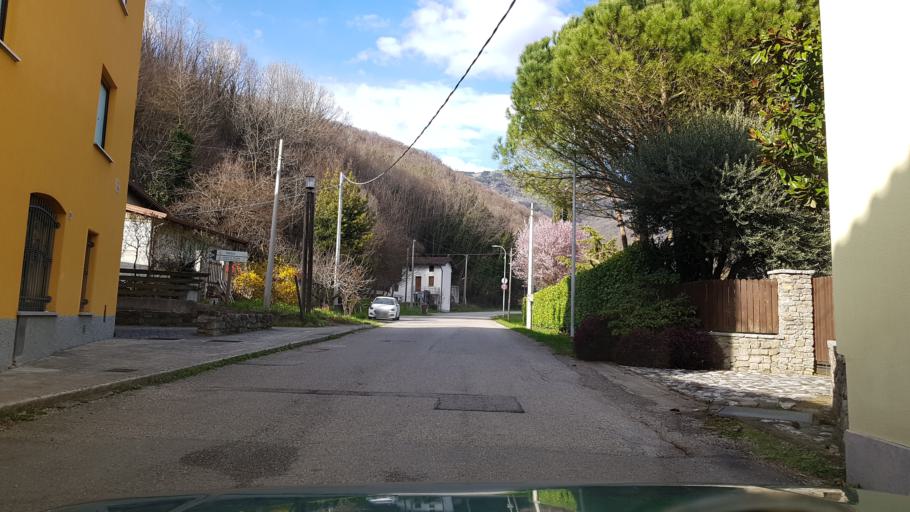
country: IT
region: Friuli Venezia Giulia
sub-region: Provincia di Udine
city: Faedis
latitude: 46.1565
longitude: 13.3504
